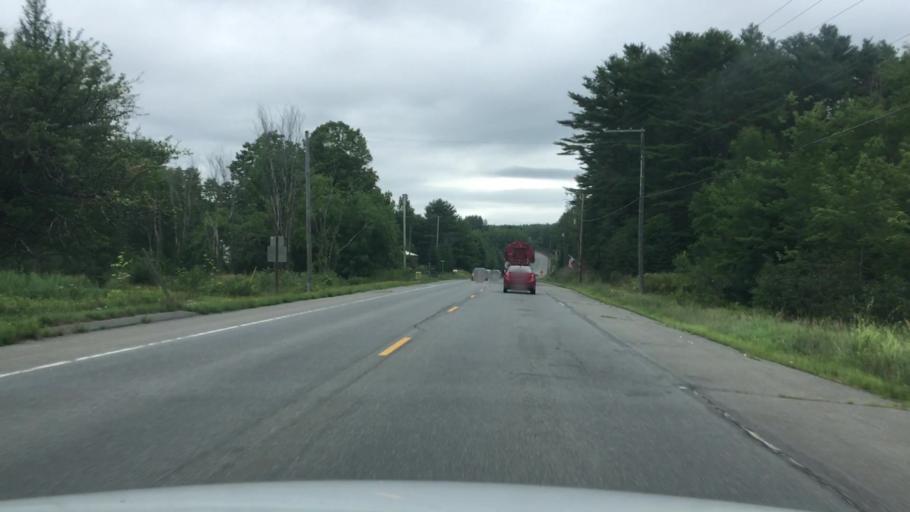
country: US
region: Maine
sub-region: Hancock County
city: Franklin
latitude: 44.8338
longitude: -68.3606
